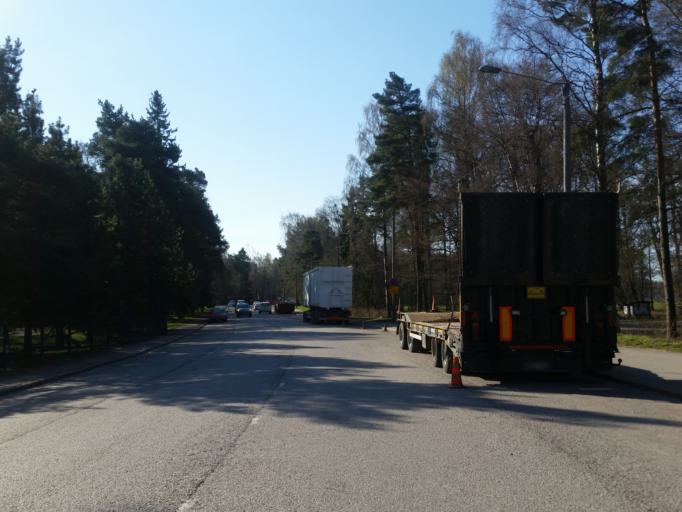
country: FI
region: Uusimaa
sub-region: Helsinki
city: Teekkarikylae
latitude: 60.1567
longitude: 24.8739
